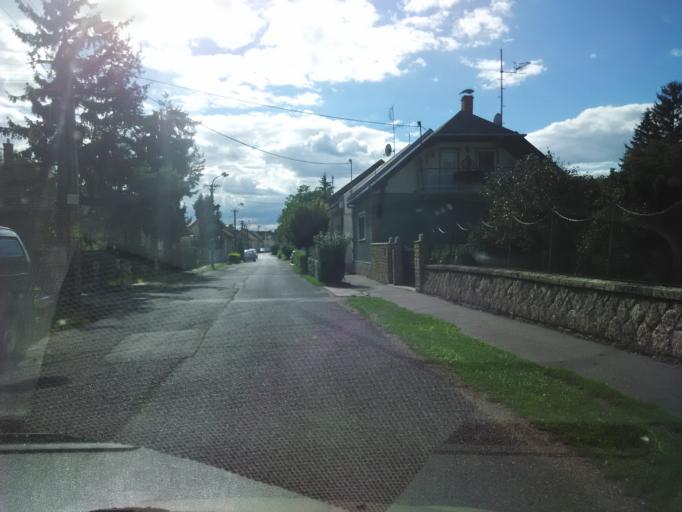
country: SK
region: Nitriansky
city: Levice
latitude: 48.2198
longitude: 18.6119
